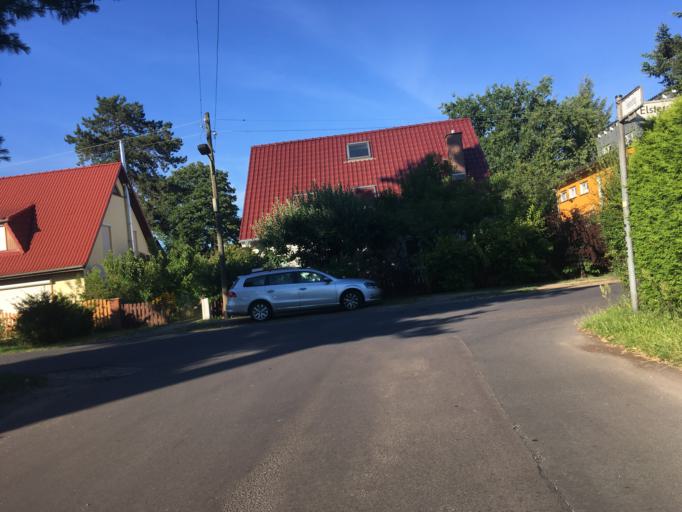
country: DE
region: Berlin
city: Grunau
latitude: 52.4263
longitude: 13.5686
